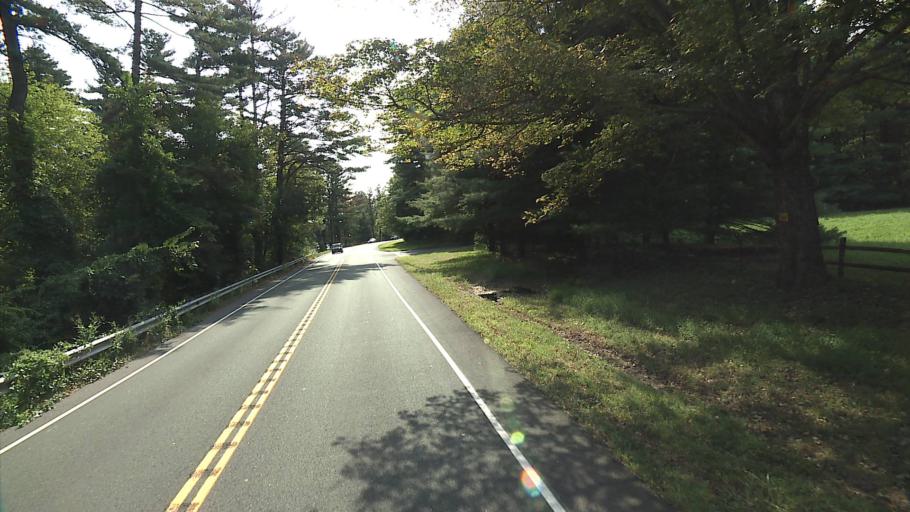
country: US
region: Connecticut
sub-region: Fairfield County
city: Fairfield
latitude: 41.2086
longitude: -73.2869
